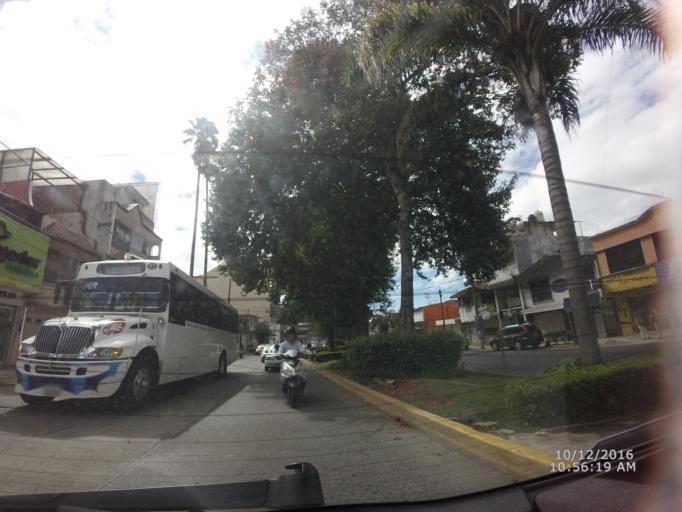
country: TR
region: Sivas
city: Karayun
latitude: 39.6720
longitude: 37.2404
